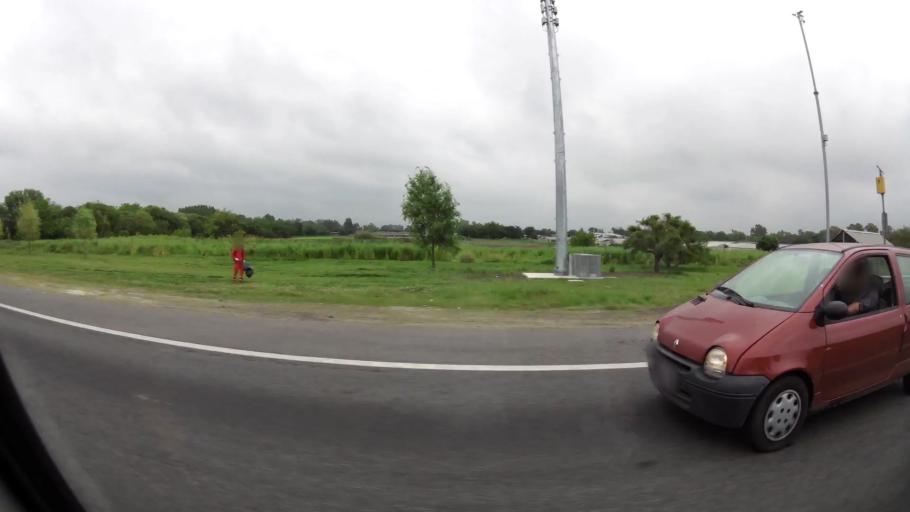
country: AR
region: Buenos Aires
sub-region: Partido de Quilmes
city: Quilmes
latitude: -34.7967
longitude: -58.1316
